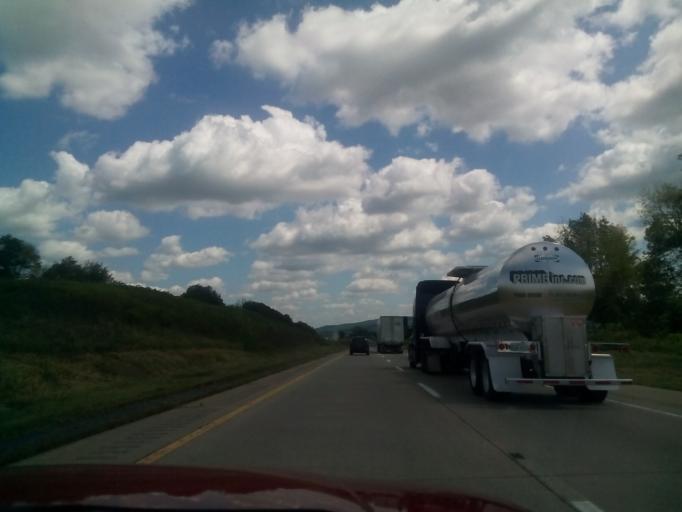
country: US
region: Pennsylvania
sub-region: Northumberland County
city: Riverside
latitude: 40.9898
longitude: -76.6749
